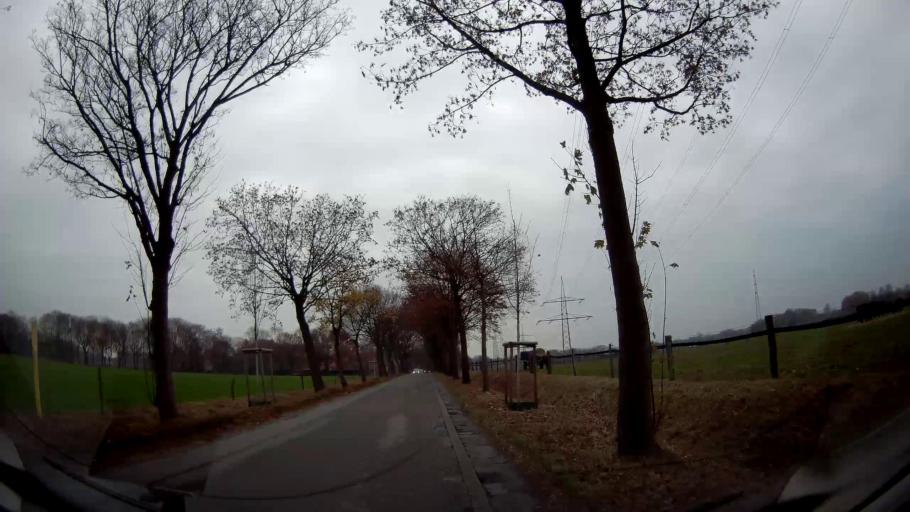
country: DE
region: North Rhine-Westphalia
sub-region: Regierungsbezirk Munster
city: Gladbeck
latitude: 51.5695
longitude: 7.0204
